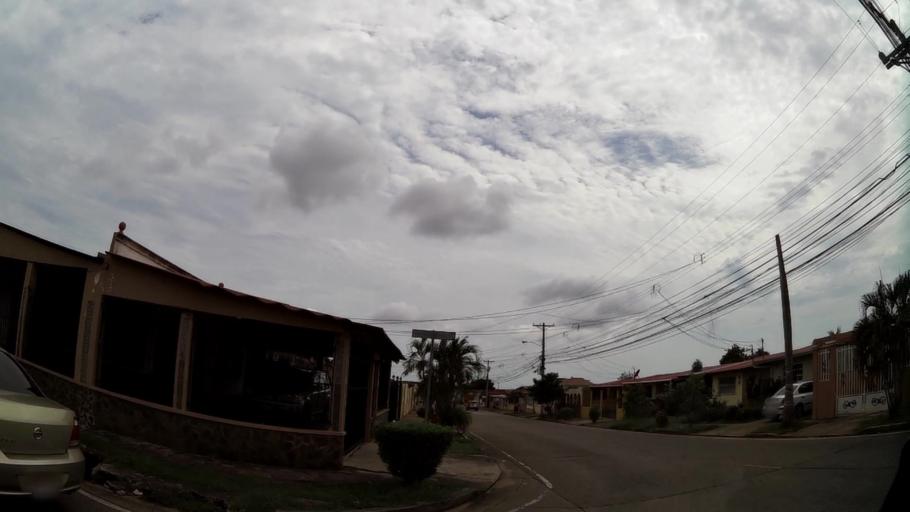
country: PA
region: Panama
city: San Miguelito
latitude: 9.0534
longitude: -79.4197
